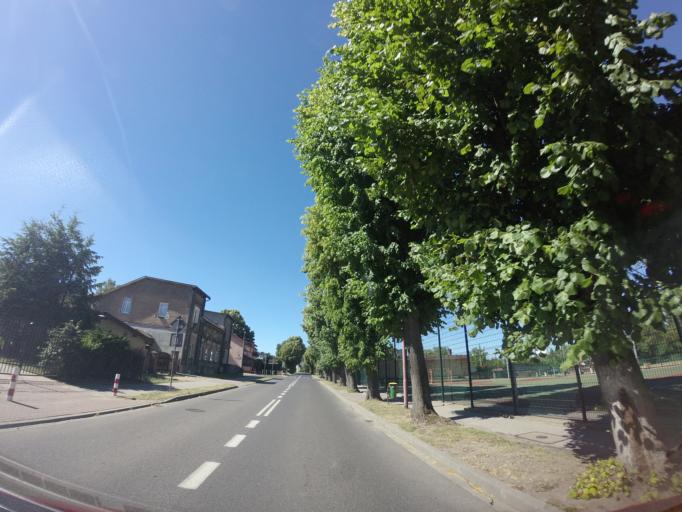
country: PL
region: West Pomeranian Voivodeship
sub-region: Powiat stargardzki
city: Dolice
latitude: 53.1896
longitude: 15.2017
